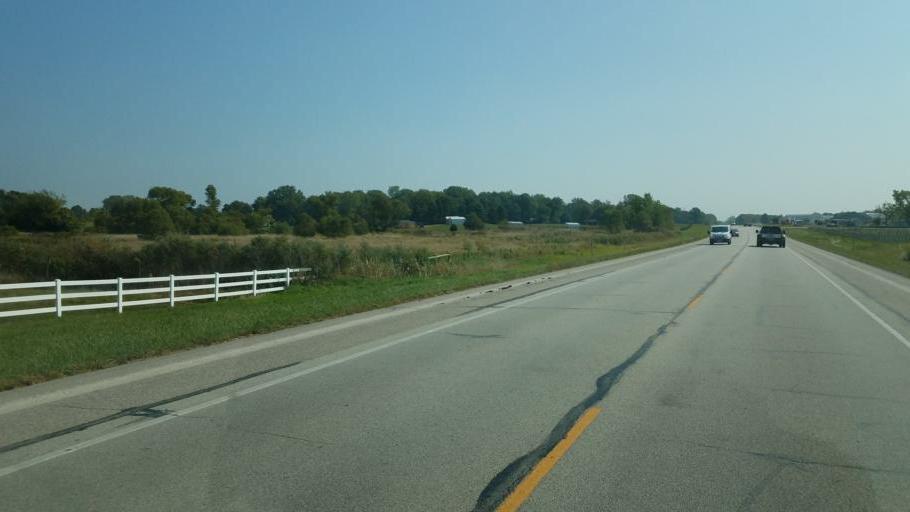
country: US
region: Indiana
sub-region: LaGrange County
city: Topeka
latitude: 41.6497
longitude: -85.5654
